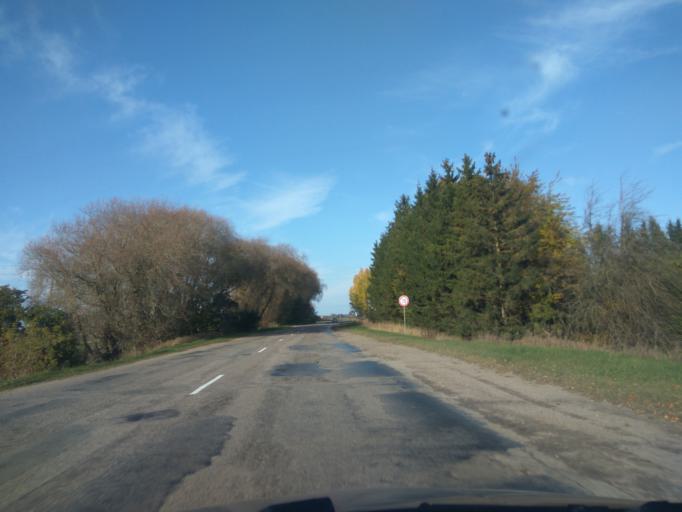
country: LV
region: Ventspils
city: Ventspils
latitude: 57.3064
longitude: 21.5579
